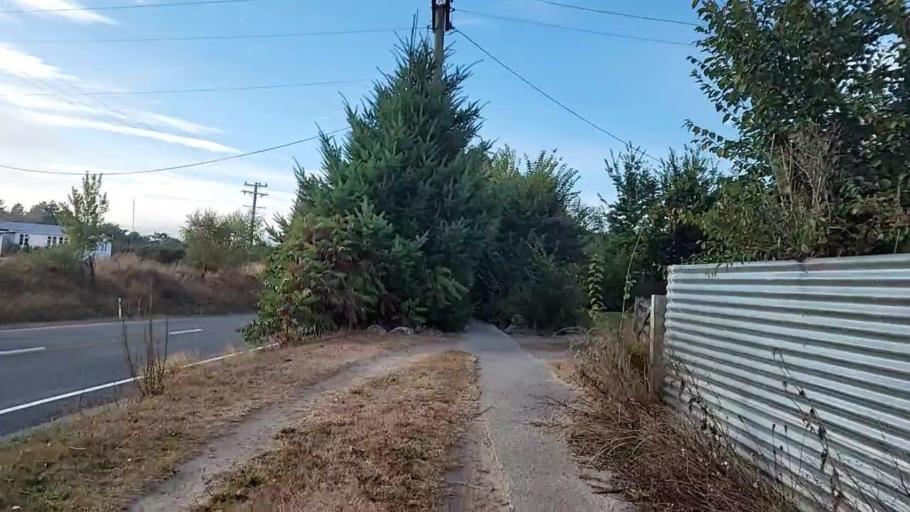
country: NZ
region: Southland
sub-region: Gore District
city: Gore
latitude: -45.6408
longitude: 169.3724
